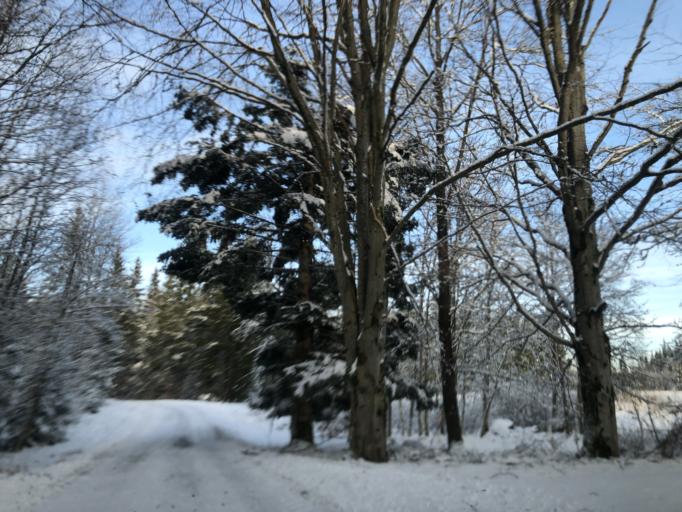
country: SE
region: Vaestra Goetaland
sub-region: Ulricehamns Kommun
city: Ulricehamn
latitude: 57.7459
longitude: 13.5079
